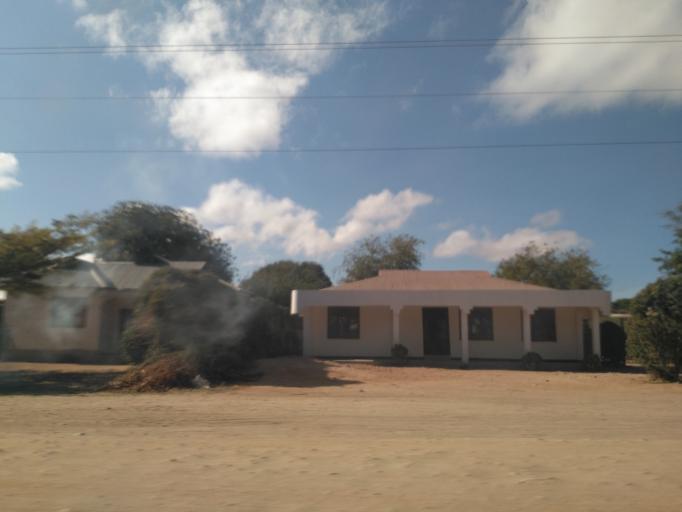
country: TZ
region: Dodoma
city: Dodoma
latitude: -6.1864
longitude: 35.7367
